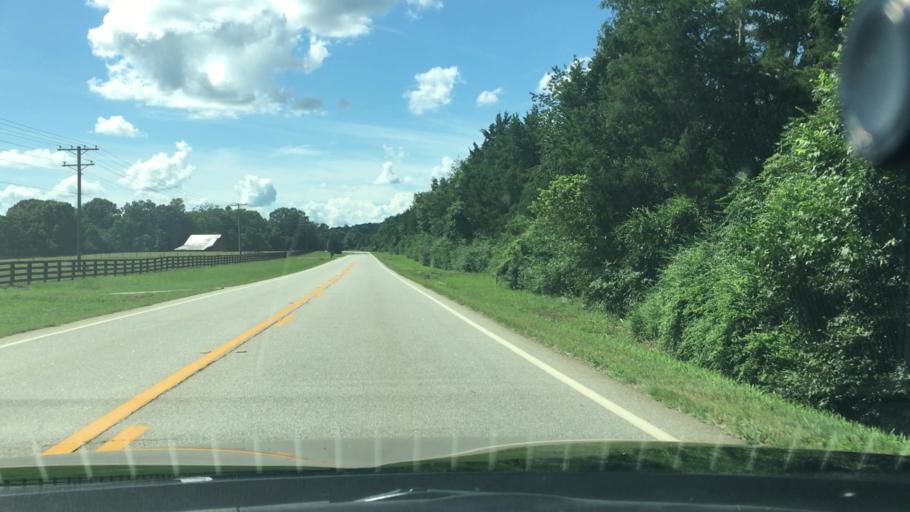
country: US
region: Georgia
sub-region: Jasper County
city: Monticello
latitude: 33.3130
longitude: -83.7477
